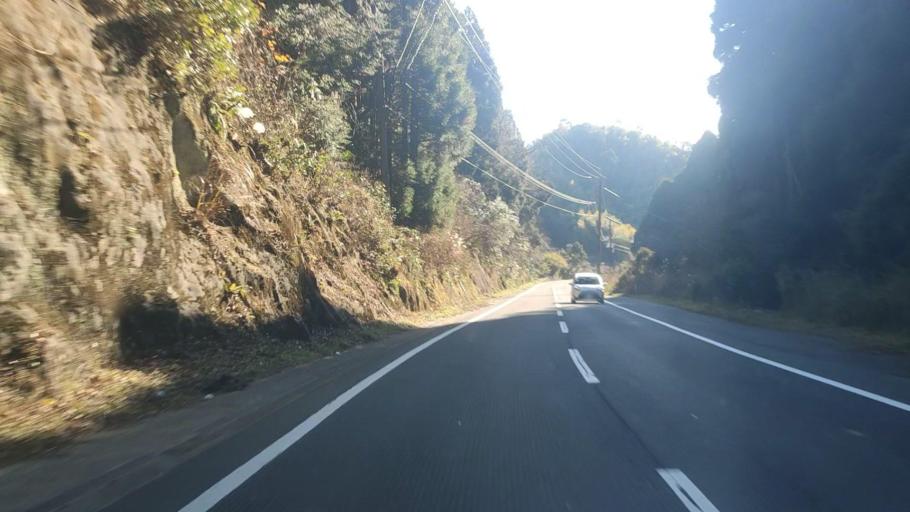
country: JP
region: Saga Prefecture
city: Kanzakimachi-kanzaki
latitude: 33.3951
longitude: 130.2713
